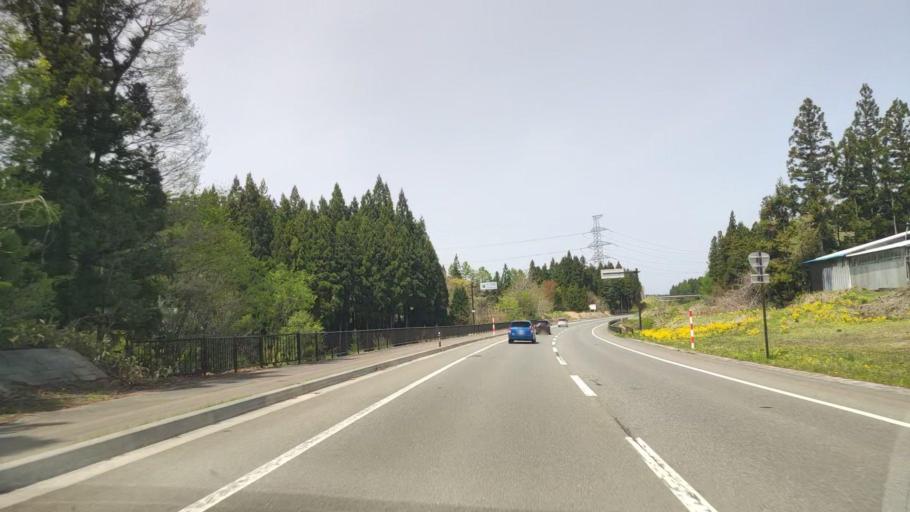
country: JP
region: Aomori
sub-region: Misawa Shi
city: Inuotose
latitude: 40.6801
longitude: 141.1712
